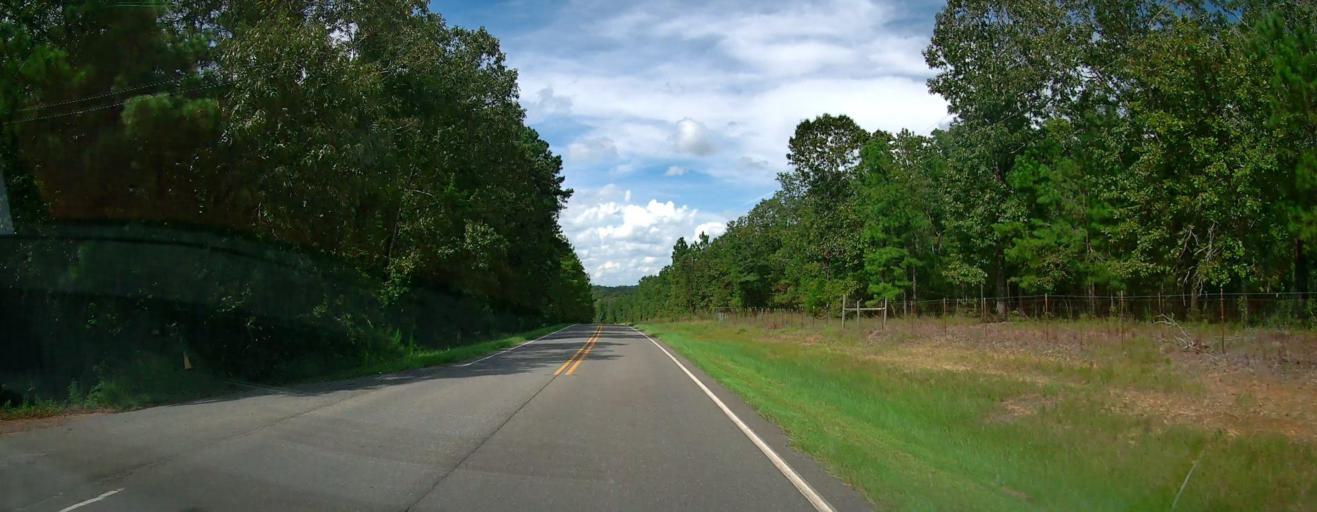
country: US
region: Georgia
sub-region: Taylor County
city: Butler
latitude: 32.5242
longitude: -84.2063
